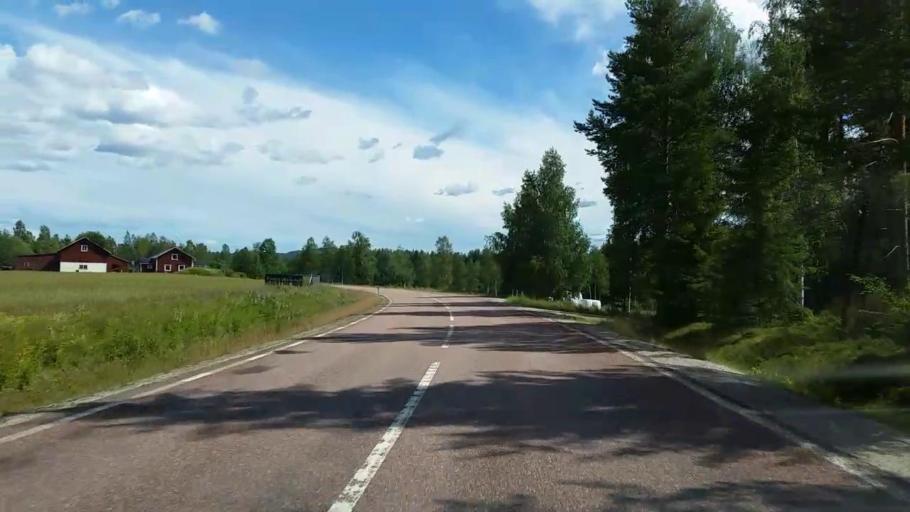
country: SE
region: Gaevleborg
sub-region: Ovanakers Kommun
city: Edsbyn
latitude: 61.3470
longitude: 15.5959
